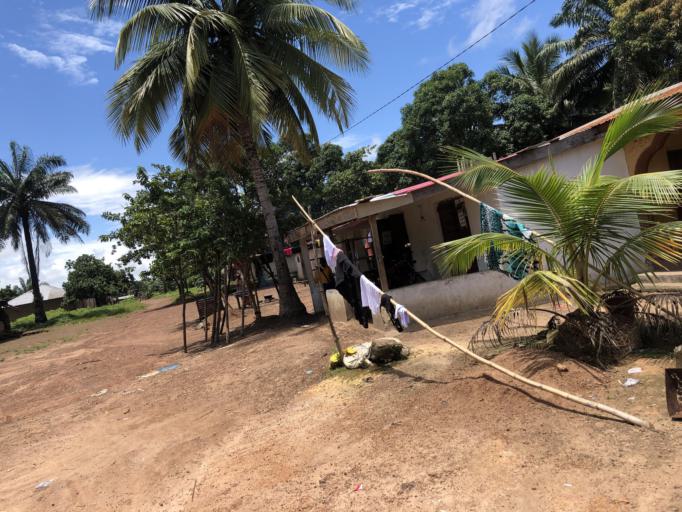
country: SL
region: Northern Province
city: Makeni
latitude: 8.8667
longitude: -12.1267
